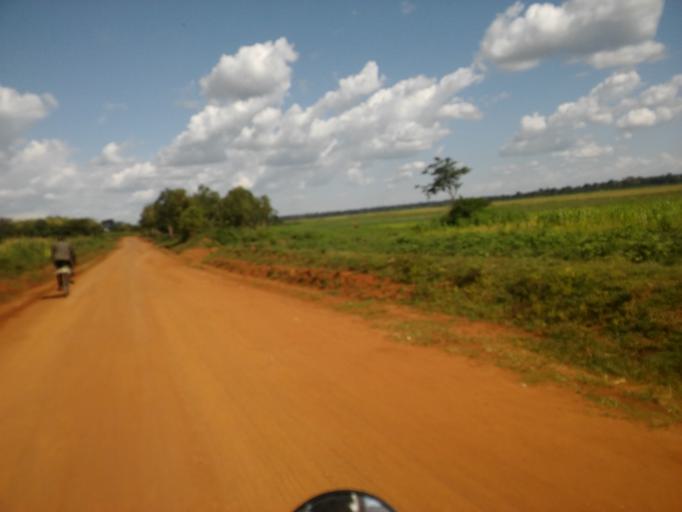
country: UG
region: Eastern Region
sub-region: Pallisa District
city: Pallisa
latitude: 1.1253
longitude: 33.7367
